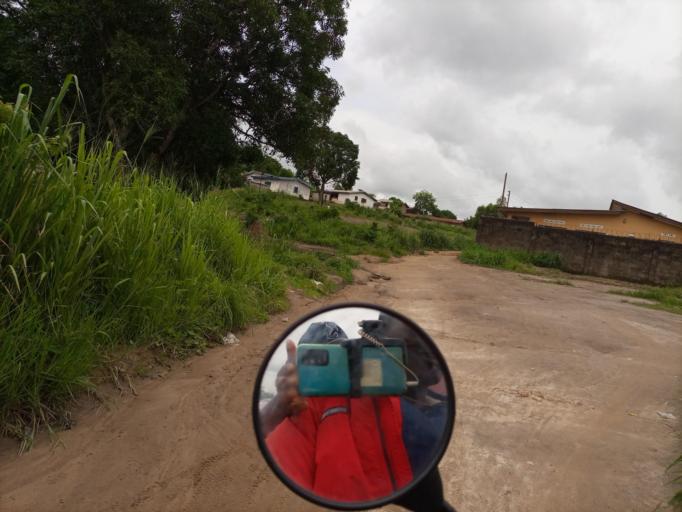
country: SL
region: Southern Province
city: Bo
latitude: 7.9475
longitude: -11.7468
